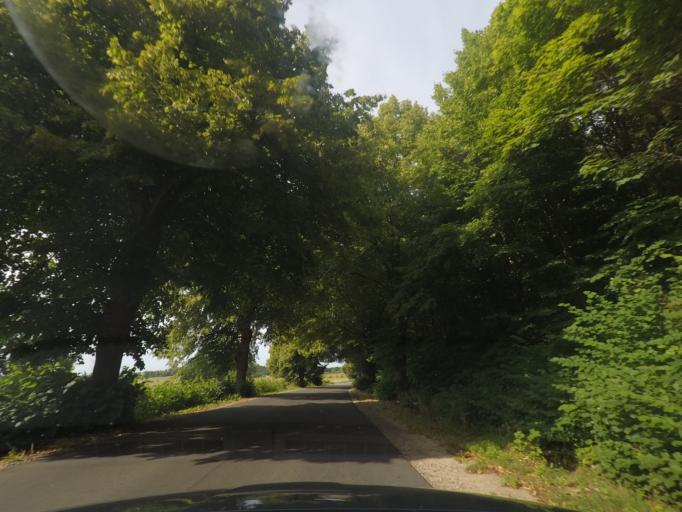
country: PL
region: Pomeranian Voivodeship
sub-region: Powiat slupski
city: Smoldzino
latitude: 54.6247
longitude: 17.1406
